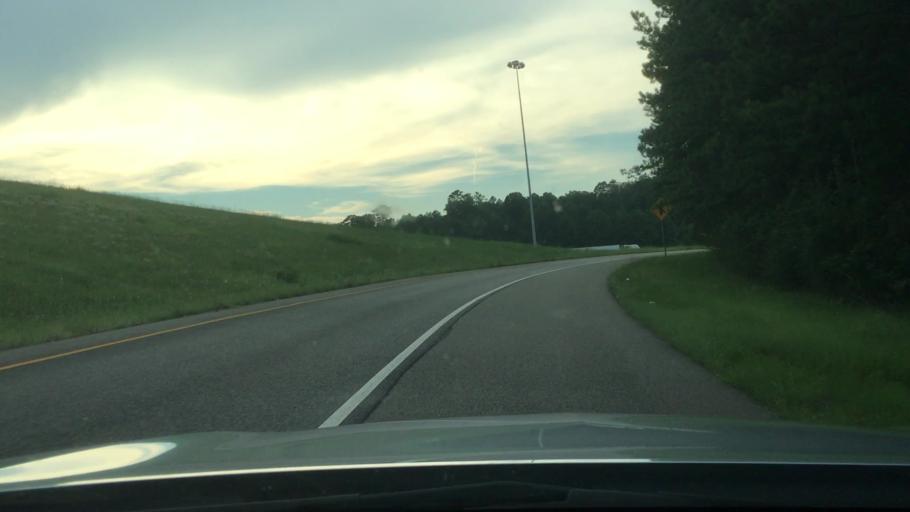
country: US
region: Alabama
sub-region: Jefferson County
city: Irondale
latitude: 33.5463
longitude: -86.6405
